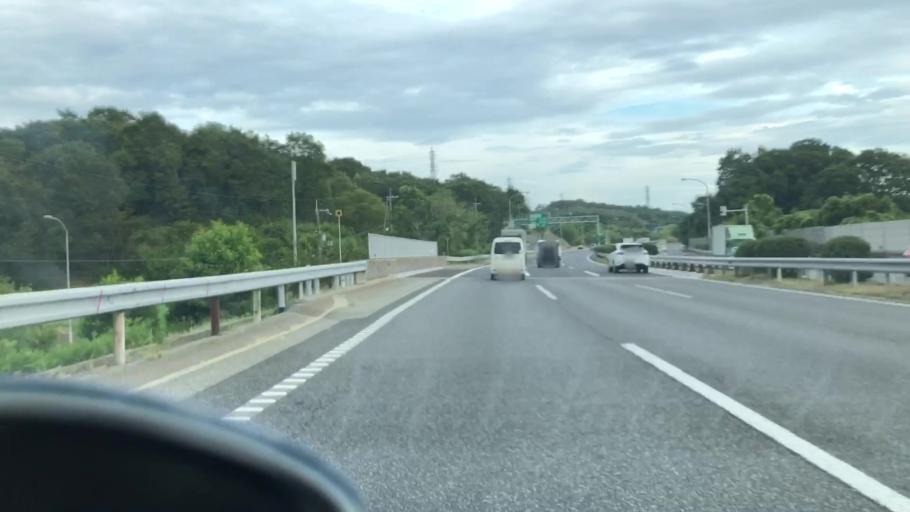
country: JP
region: Hyogo
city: Sandacho
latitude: 34.8840
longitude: 135.1818
